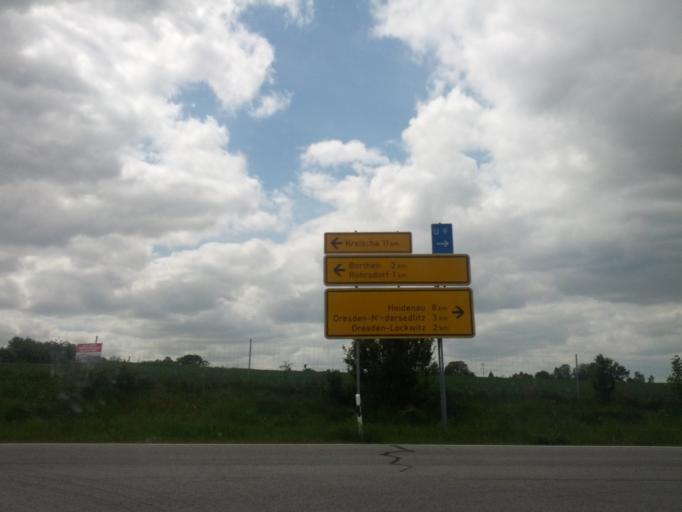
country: DE
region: Saxony
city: Dohna
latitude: 50.9739
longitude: 13.8099
